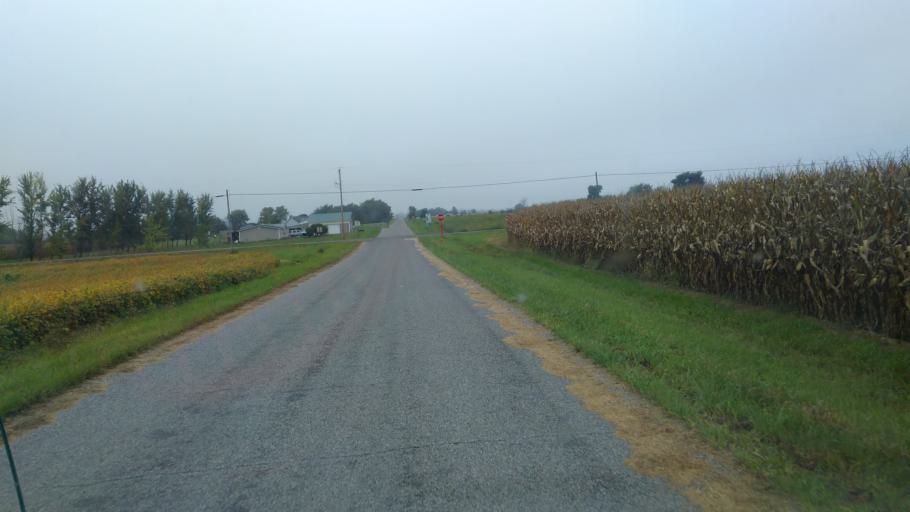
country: US
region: Ohio
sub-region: Logan County
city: Northwood
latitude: 40.5032
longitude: -83.5982
